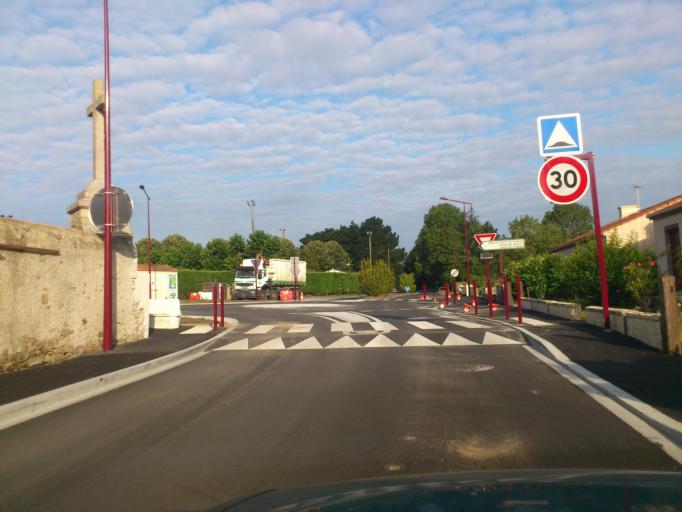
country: FR
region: Pays de la Loire
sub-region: Departement de la Loire-Atlantique
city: Saint-Hilaire-de-Clisson
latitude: 47.0615
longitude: -1.3116
